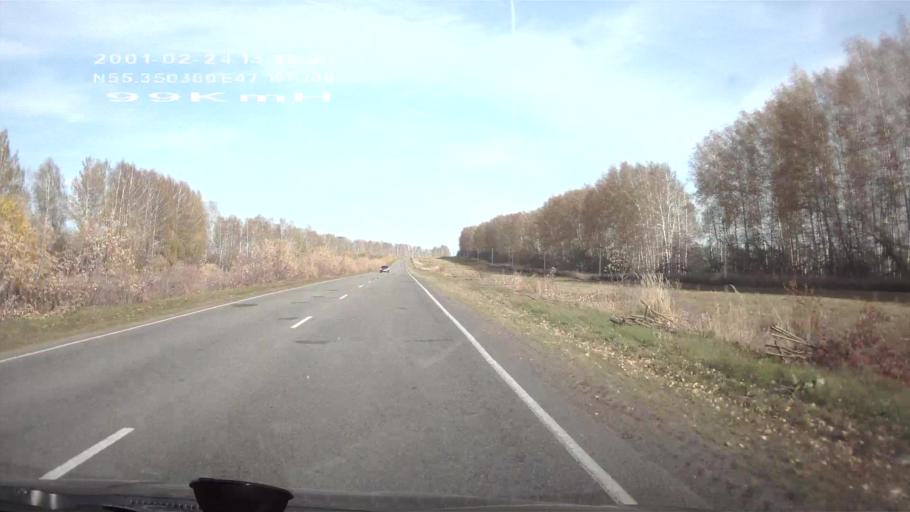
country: RU
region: Chuvashia
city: Ibresi
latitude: 55.3502
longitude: 47.1900
